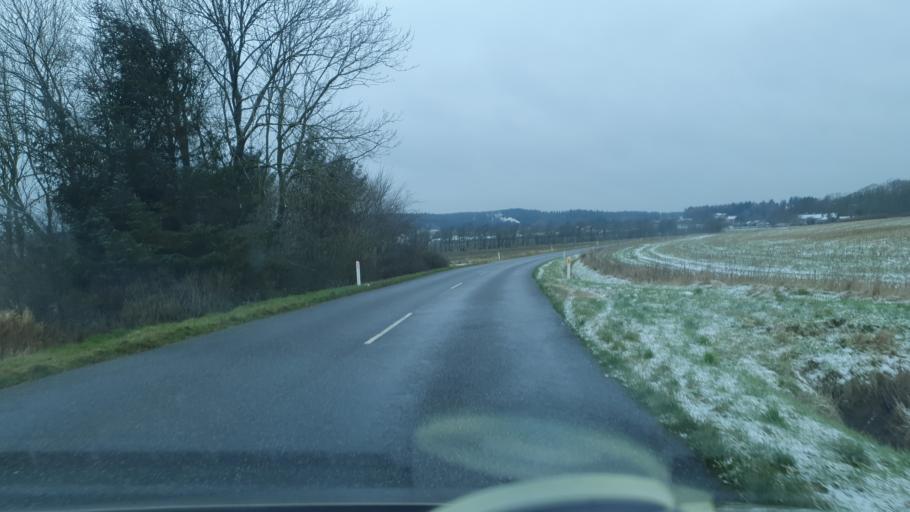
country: DK
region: North Denmark
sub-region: Jammerbugt Kommune
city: Brovst
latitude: 57.1273
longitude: 9.4750
